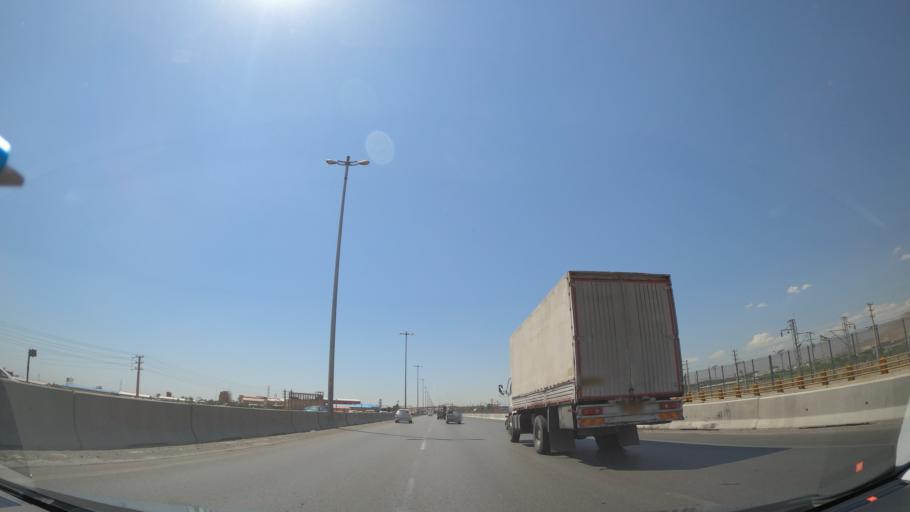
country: IR
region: Alborz
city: Karaj
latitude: 35.9055
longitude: 50.8466
